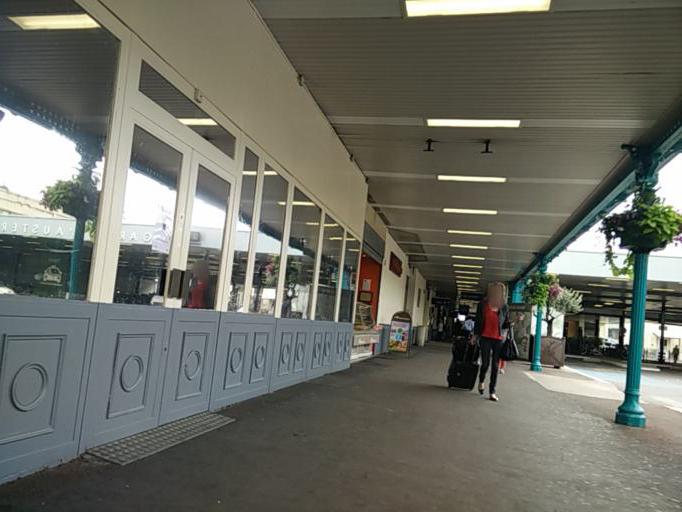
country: FR
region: Ile-de-France
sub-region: Paris
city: Paris
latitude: 48.8419
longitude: 2.3650
